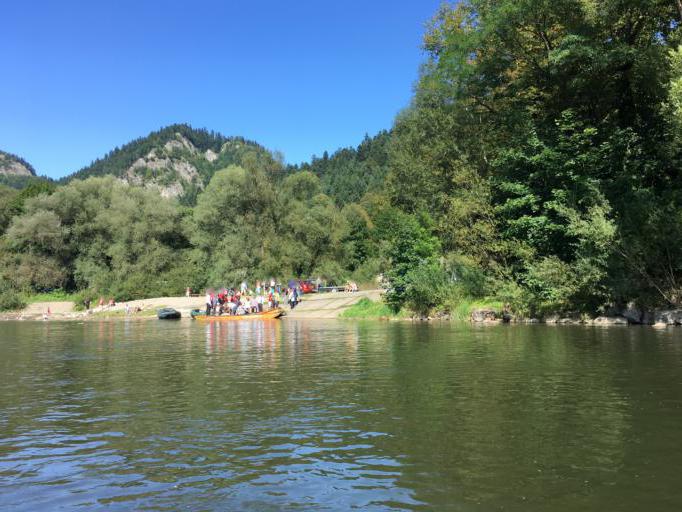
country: PL
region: Lesser Poland Voivodeship
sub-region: Powiat nowotarski
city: Kroscienko nad Dunajcem
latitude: 49.3996
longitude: 20.4148
